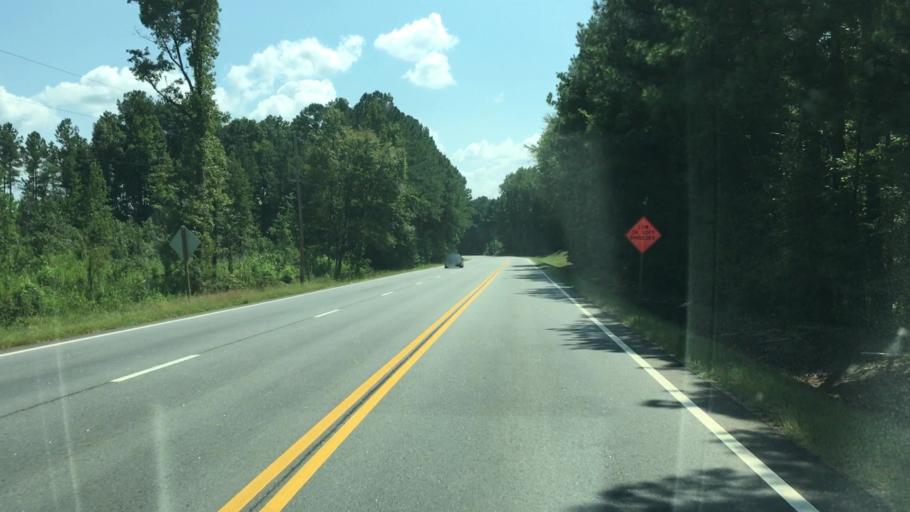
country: US
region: Georgia
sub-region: Oconee County
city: Watkinsville
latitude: 33.7337
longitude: -83.4300
